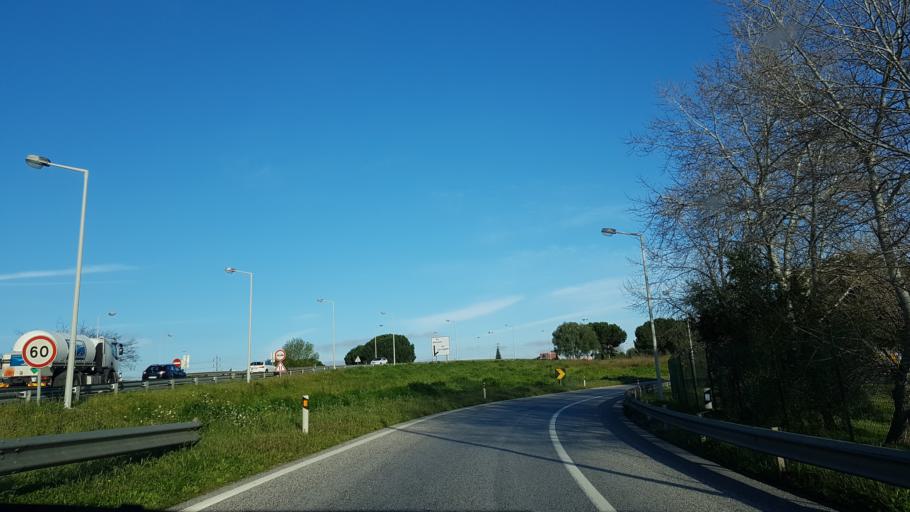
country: PT
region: Lisbon
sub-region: Alenquer
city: Carregado
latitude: 39.0257
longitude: -8.9700
